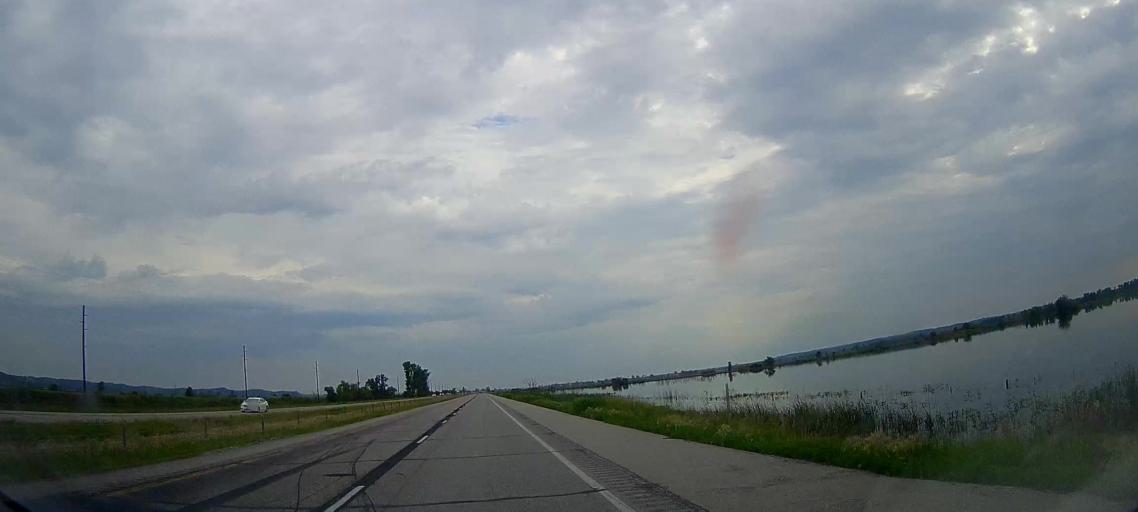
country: US
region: Iowa
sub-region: Harrison County
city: Missouri Valley
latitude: 41.4617
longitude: -95.8998
